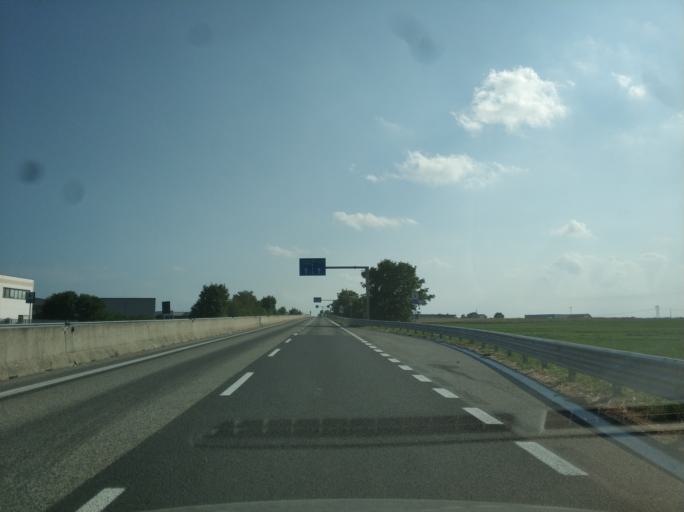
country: IT
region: Piedmont
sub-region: Provincia di Cuneo
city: Roreto
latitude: 44.6729
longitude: 7.8266
